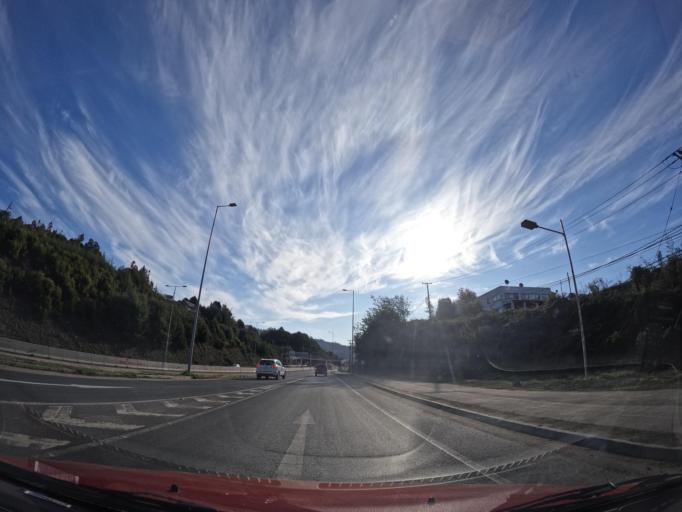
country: CL
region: Biobio
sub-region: Provincia de Concepcion
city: Penco
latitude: -36.8297
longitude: -72.9222
